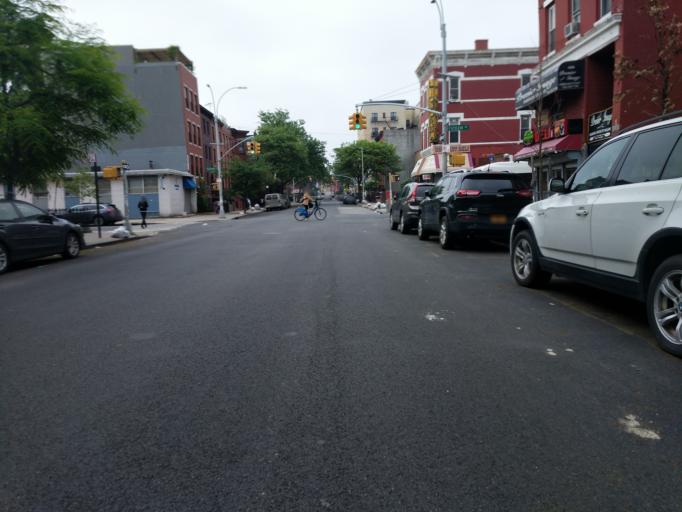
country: US
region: New York
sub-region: Kings County
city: Brooklyn
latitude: 40.6837
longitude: -73.9562
